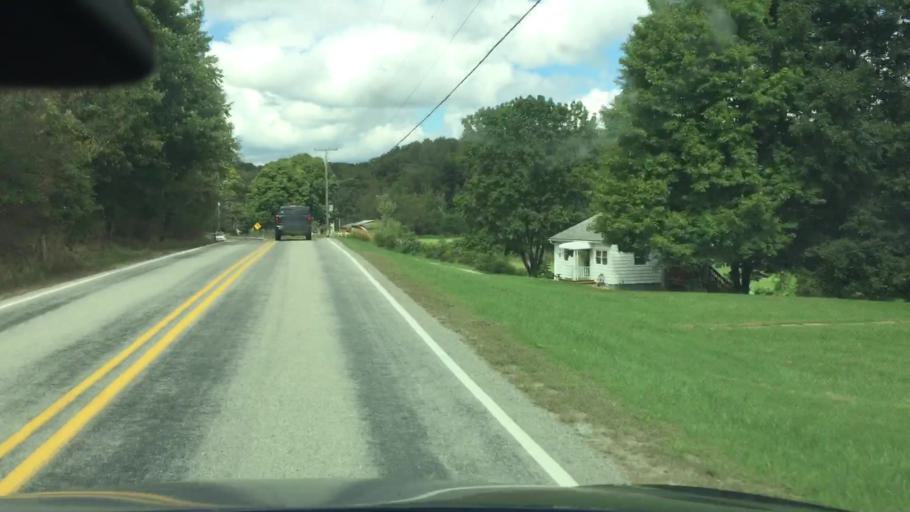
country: US
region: Pennsylvania
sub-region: Allegheny County
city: Curtisville
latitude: 40.6842
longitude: -79.8317
